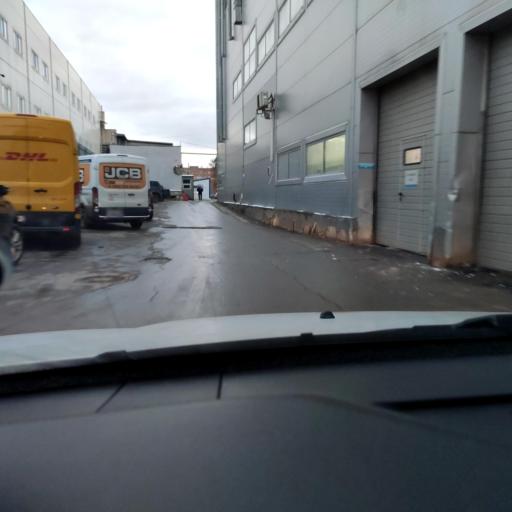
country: RU
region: Samara
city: Samara
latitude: 53.2392
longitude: 50.2452
